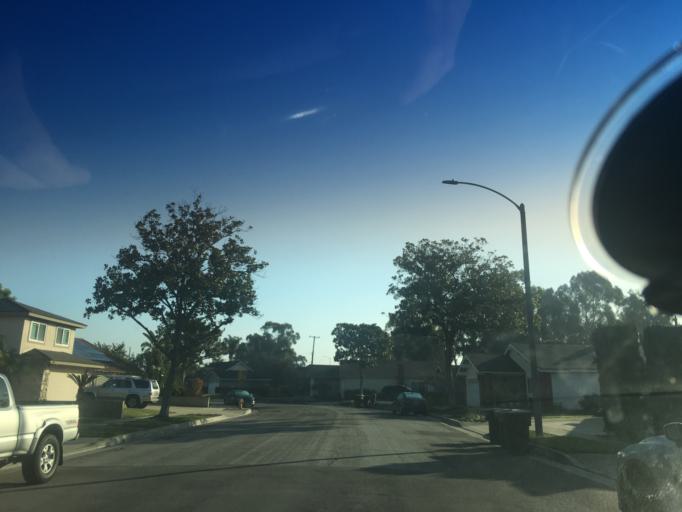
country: US
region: California
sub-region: Orange County
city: Anaheim
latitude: 33.8191
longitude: -117.8795
